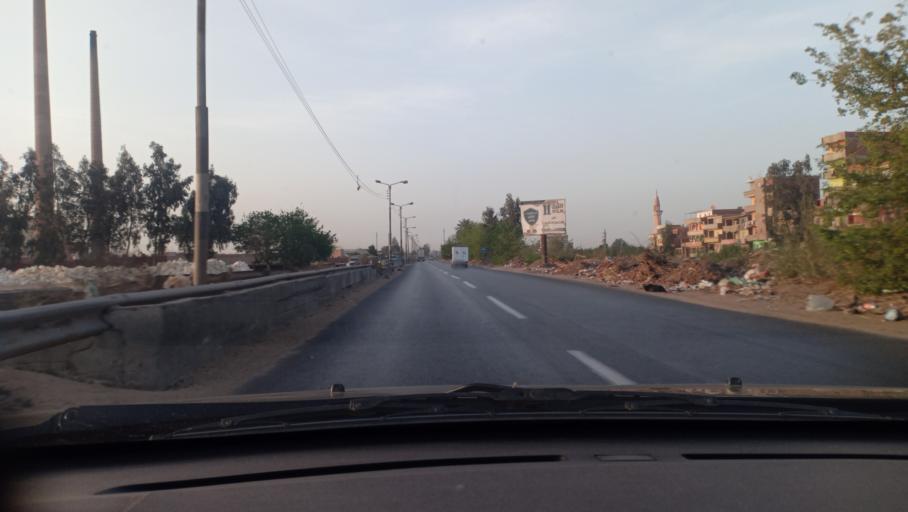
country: EG
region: Muhafazat al Gharbiyah
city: Zifta
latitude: 30.6142
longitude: 31.2767
